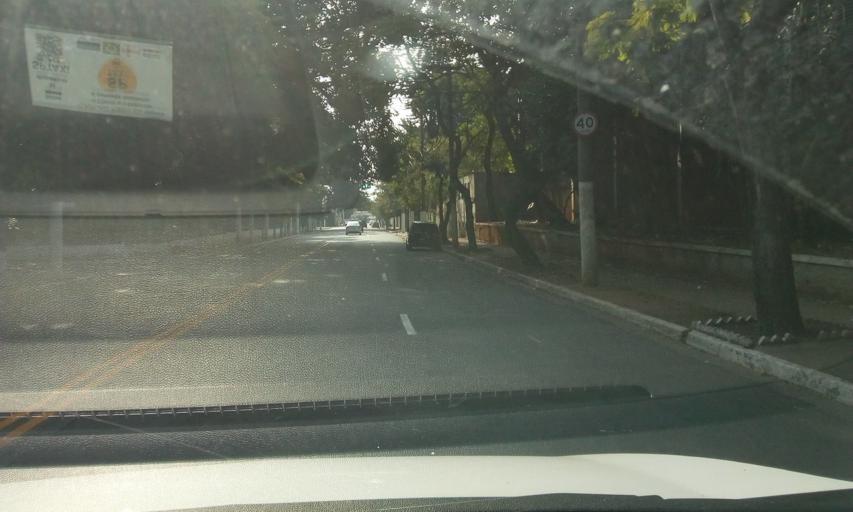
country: BR
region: Sao Paulo
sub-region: Sao Paulo
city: Sao Paulo
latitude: -23.5483
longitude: -46.5970
